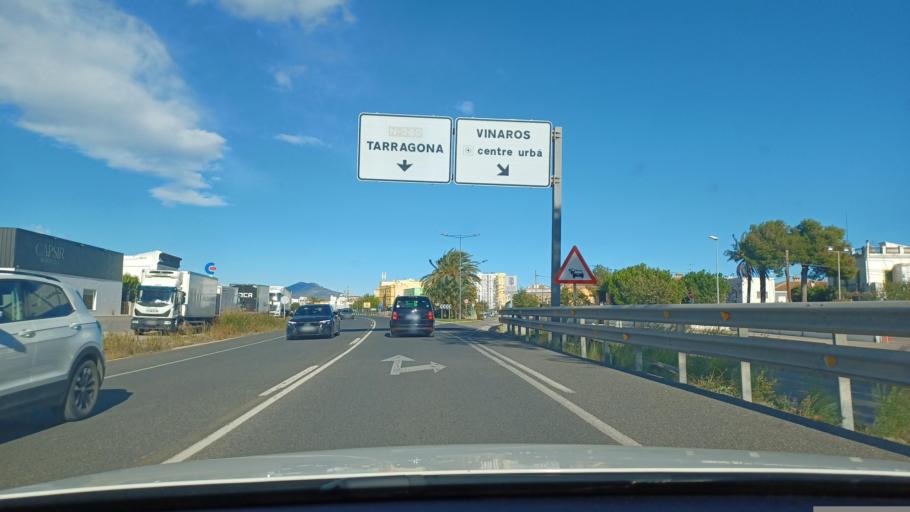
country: ES
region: Valencia
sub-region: Provincia de Castello
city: Vinaros
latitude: 40.4616
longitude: 0.4628
